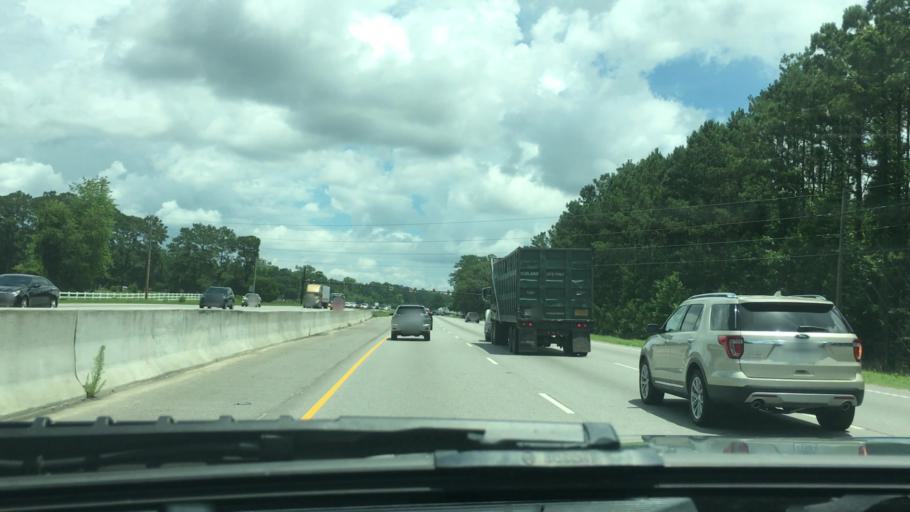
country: US
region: South Carolina
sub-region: Beaufort County
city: Bluffton
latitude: 32.2893
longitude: -80.9263
